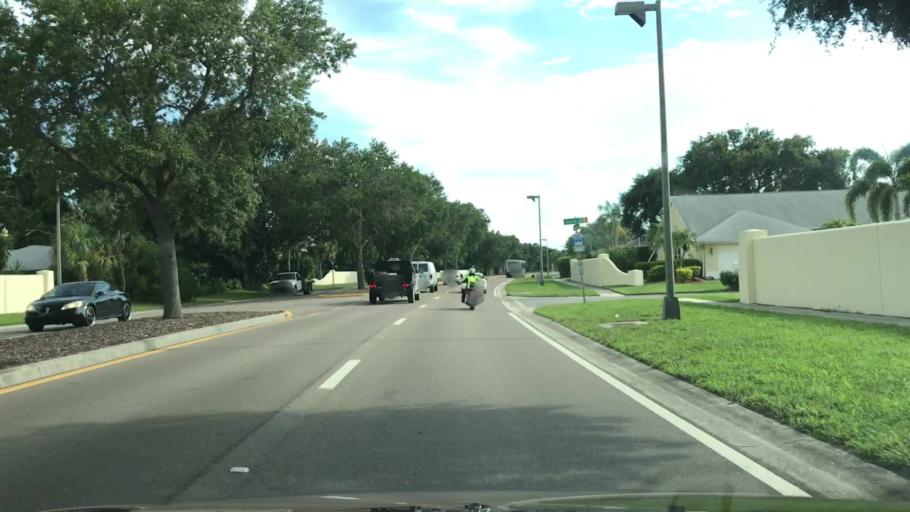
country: US
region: Florida
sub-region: Sarasota County
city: Plantation
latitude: 27.0671
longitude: -82.3905
